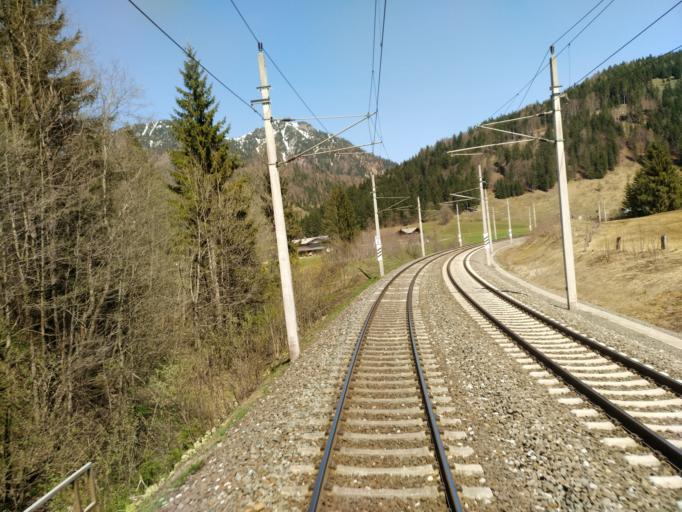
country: AT
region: Tyrol
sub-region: Politischer Bezirk Kitzbuhel
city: Hochfilzen
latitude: 47.4742
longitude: 12.6115
